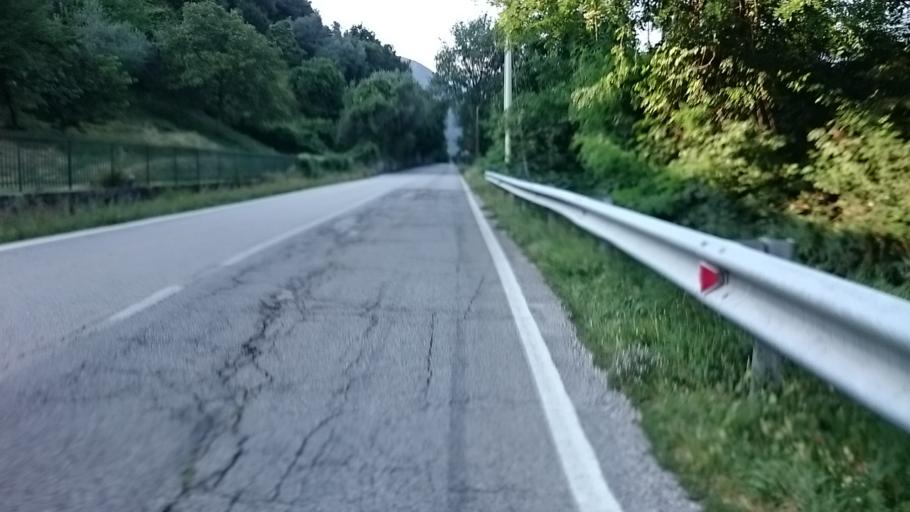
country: IT
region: Veneto
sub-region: Provincia di Vicenza
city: Campese
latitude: 45.7928
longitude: 11.7148
